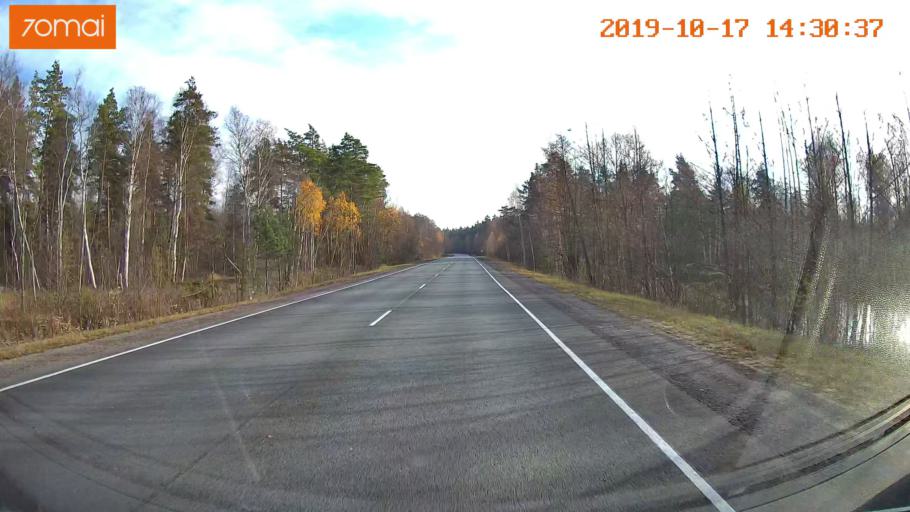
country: RU
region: Rjazan
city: Solotcha
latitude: 54.9454
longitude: 39.9481
